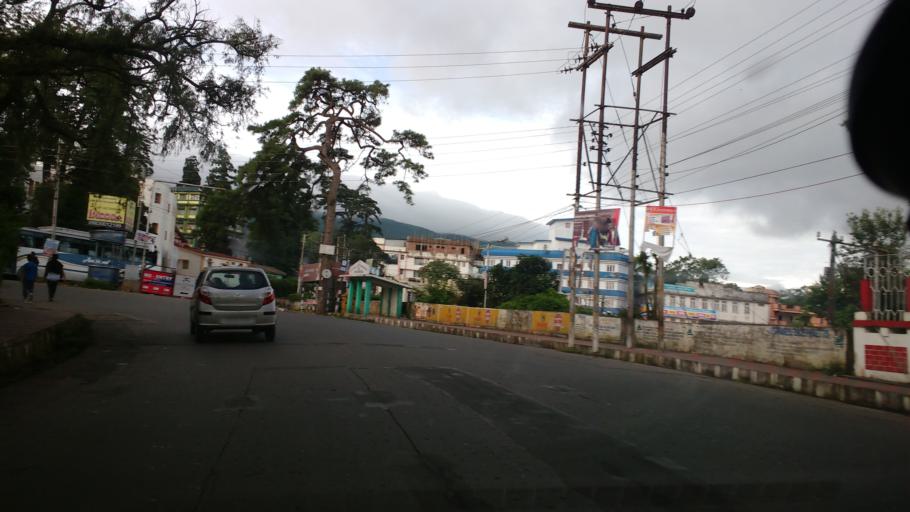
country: IN
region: Meghalaya
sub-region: East Khasi Hills
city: Shillong
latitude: 25.5738
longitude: 91.8852
